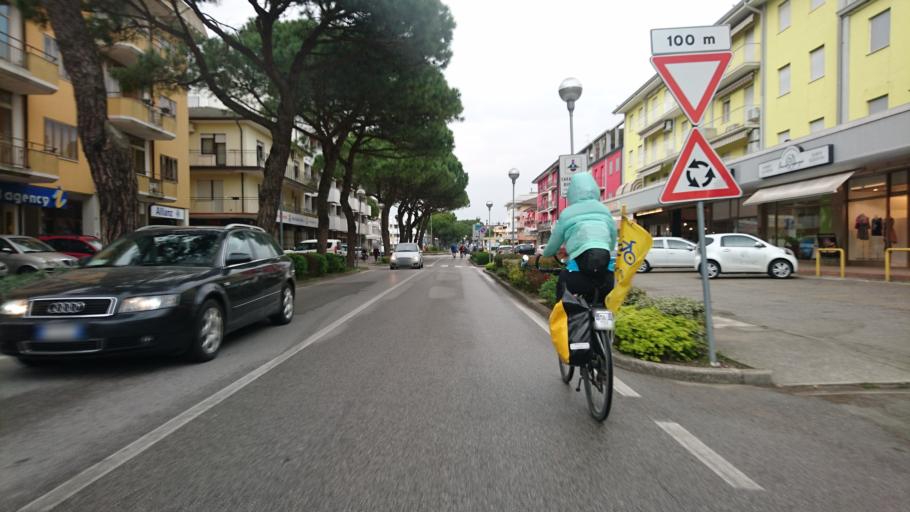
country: IT
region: Veneto
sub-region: Provincia di Venezia
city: Bibione
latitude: 45.6375
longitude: 13.0615
